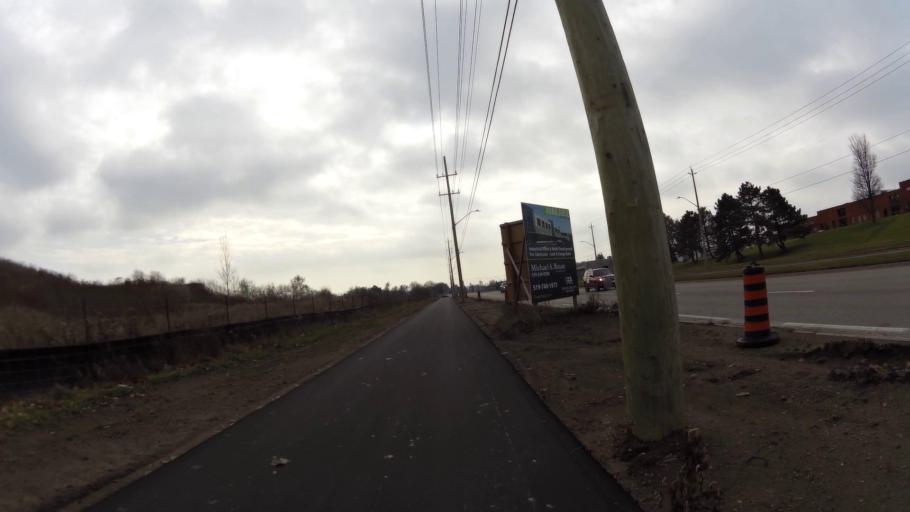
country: CA
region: Ontario
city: Kitchener
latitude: 43.4044
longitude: -80.4574
